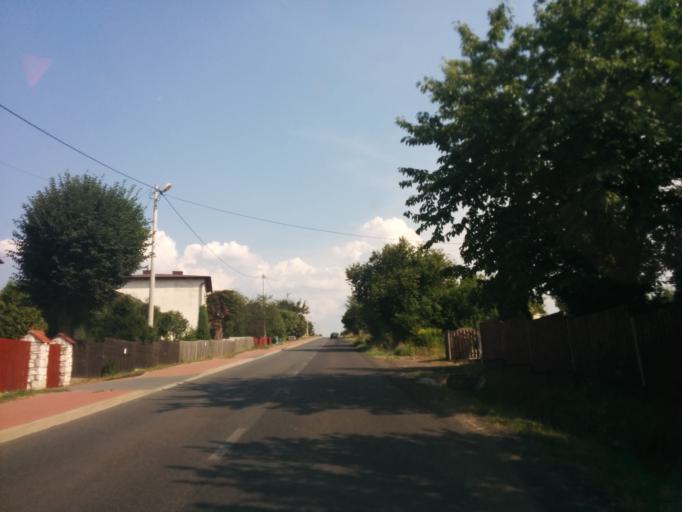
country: PL
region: Silesian Voivodeship
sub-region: Powiat myszkowski
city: Choron
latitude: 50.7121
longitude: 19.2654
